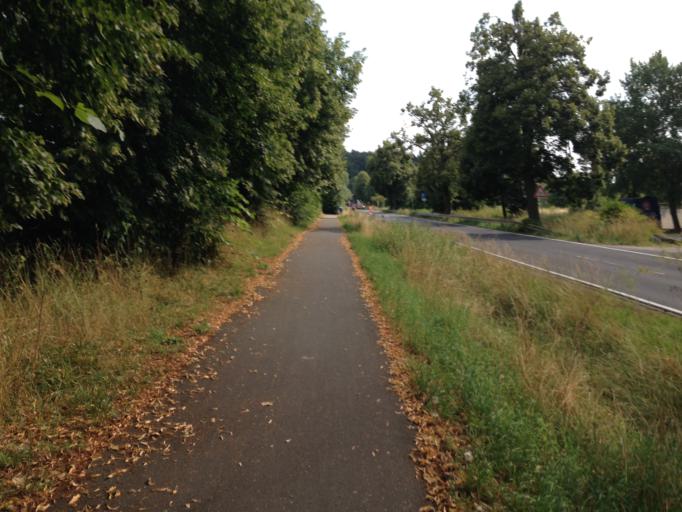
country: DE
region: Hesse
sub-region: Regierungsbezirk Giessen
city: Heuchelheim
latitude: 50.5681
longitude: 8.6285
